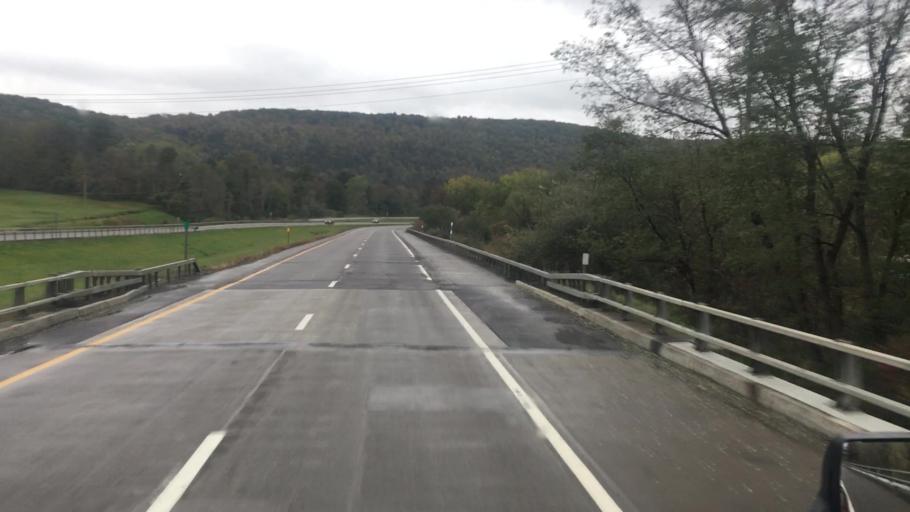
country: US
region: New York
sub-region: Tioga County
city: Apalachin
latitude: 42.0815
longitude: -76.2030
